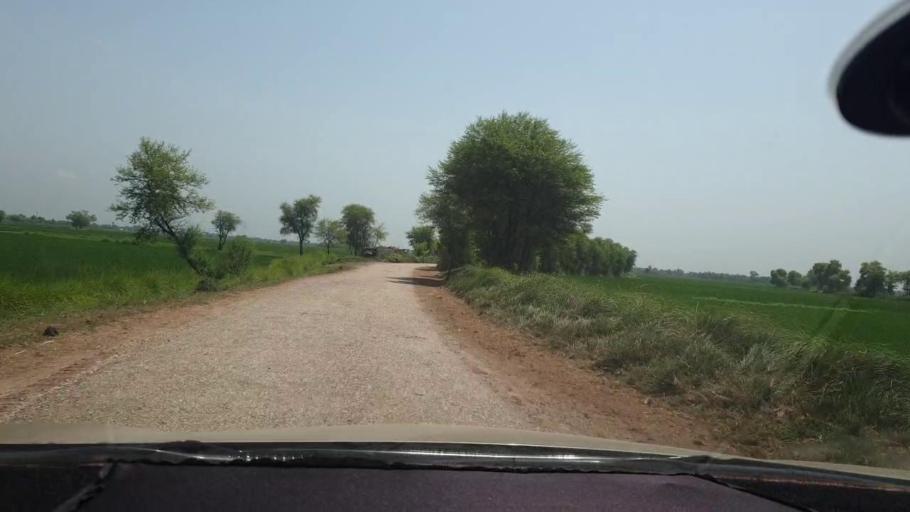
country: PK
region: Sindh
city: Kambar
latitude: 27.6854
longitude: 67.9371
